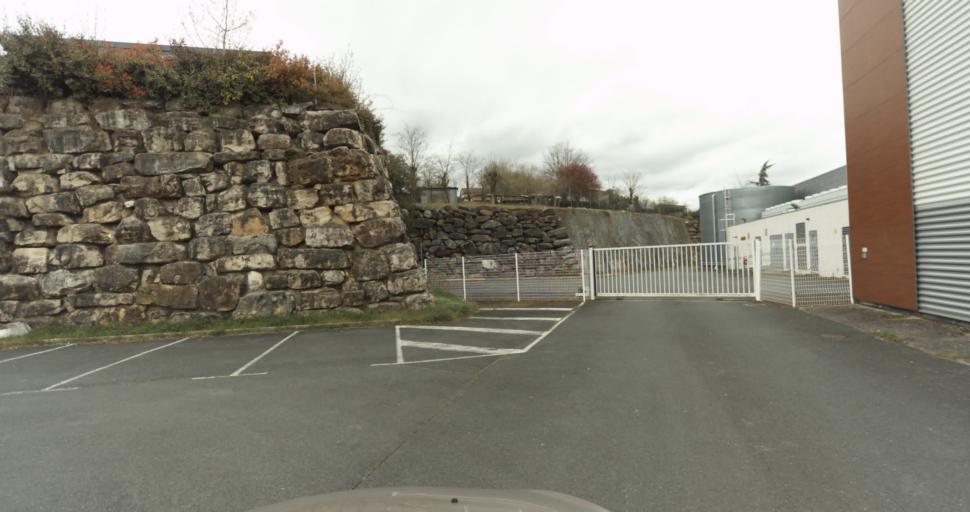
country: FR
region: Midi-Pyrenees
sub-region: Departement du Tarn
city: Puygouzon
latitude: 43.8922
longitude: 2.1676
